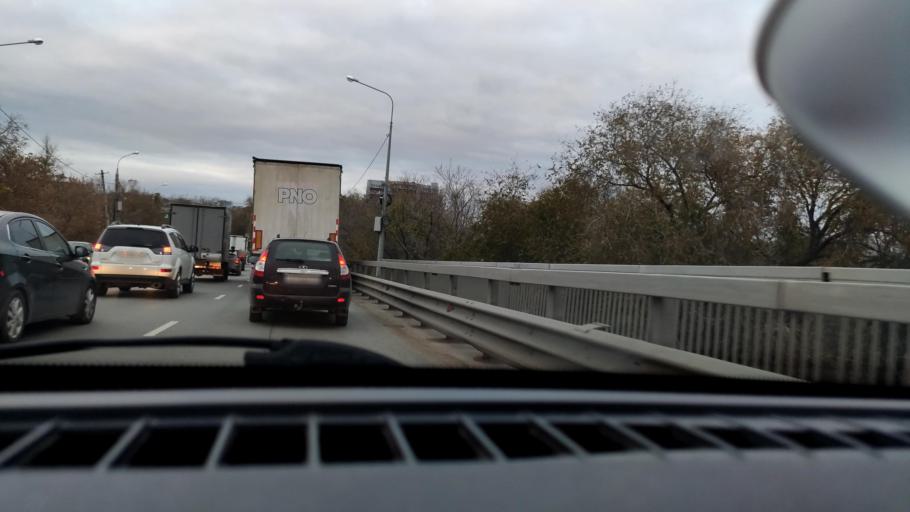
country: RU
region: Samara
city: Samara
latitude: 53.1766
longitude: 50.1934
